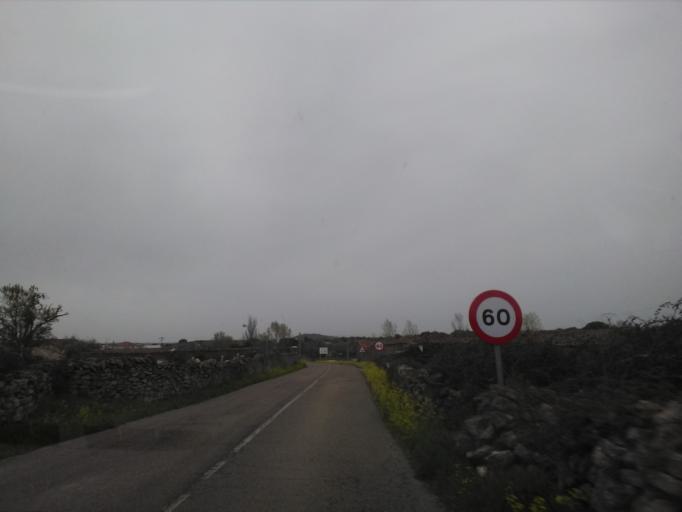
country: ES
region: Castille and Leon
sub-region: Provincia de Salamanca
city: Yecla de Yeltes
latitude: 40.9630
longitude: -6.4880
